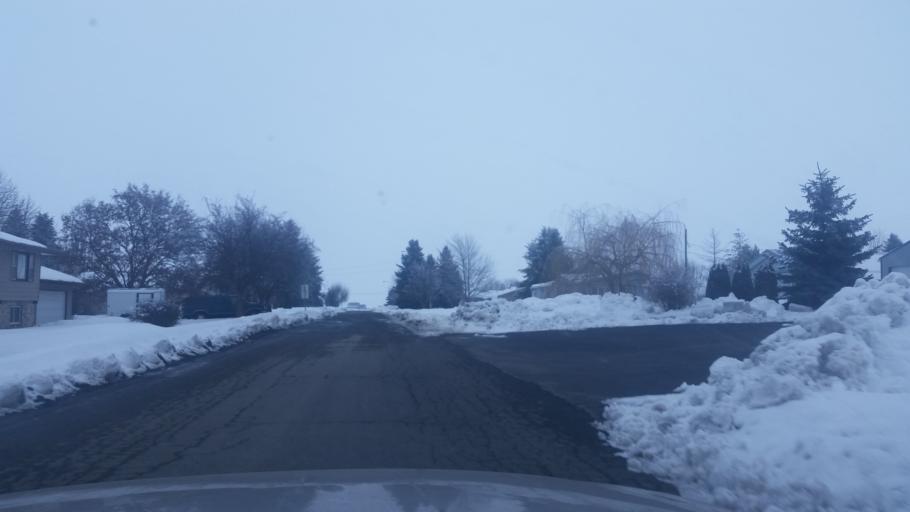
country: US
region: Washington
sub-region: Spokane County
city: Medical Lake
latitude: 47.6684
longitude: -117.8730
